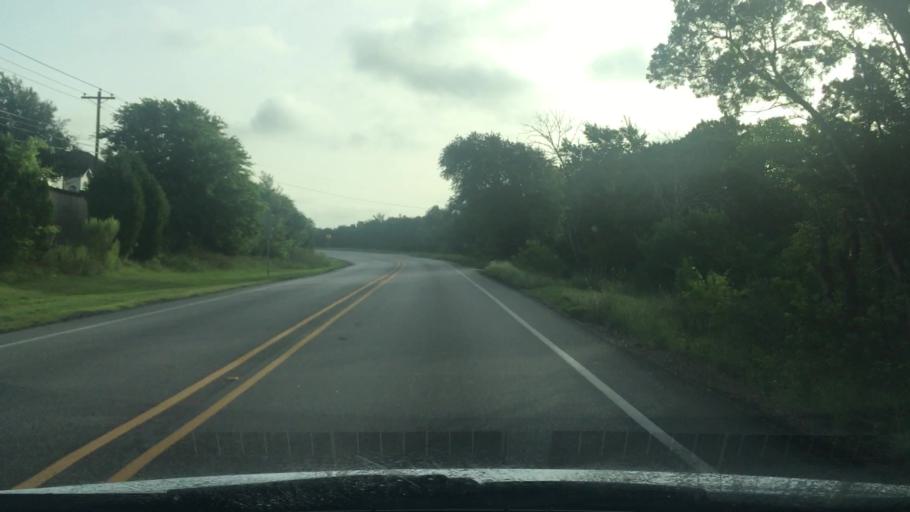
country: US
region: Texas
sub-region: Williamson County
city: Anderson Mill
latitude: 30.4535
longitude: -97.8477
